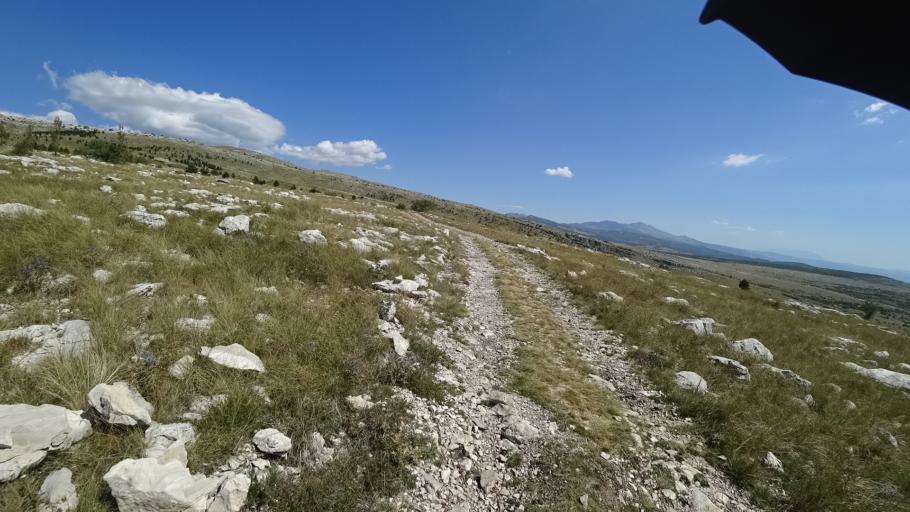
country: HR
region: Splitsko-Dalmatinska
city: Hrvace
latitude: 43.8634
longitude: 16.6406
